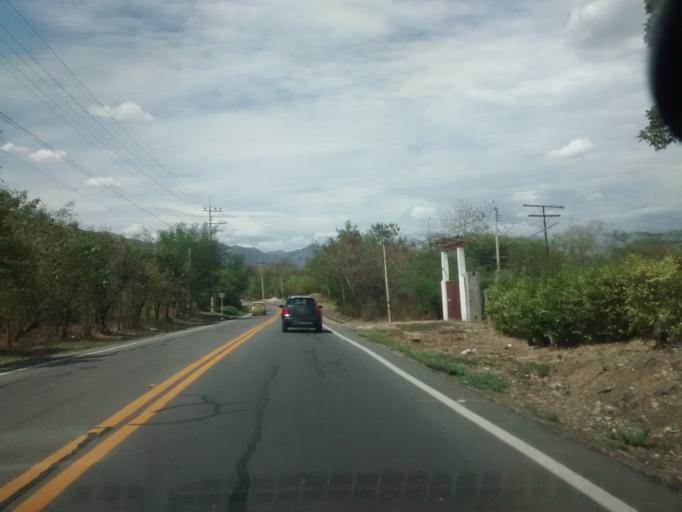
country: CO
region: Cundinamarca
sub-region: Girardot
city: Girardot City
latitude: 4.3356
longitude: -74.8052
